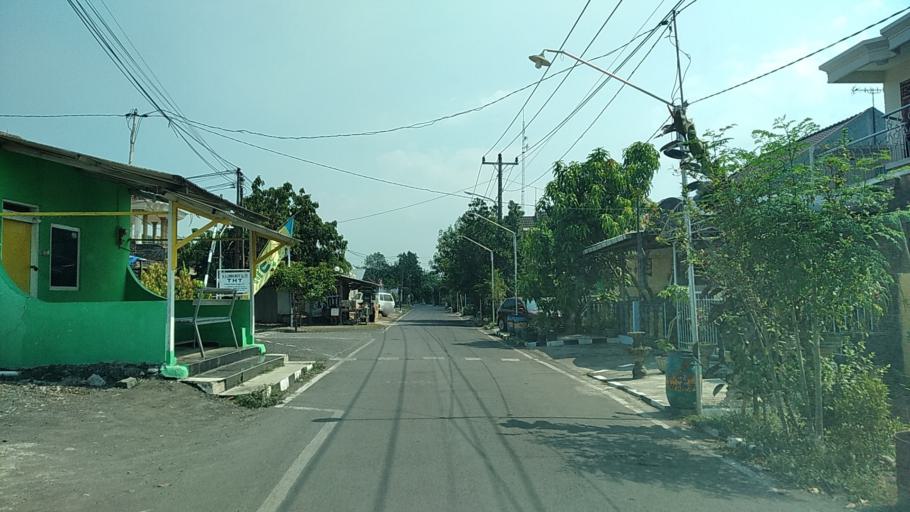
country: ID
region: Central Java
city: Mranggen
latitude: -7.0458
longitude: 110.4813
